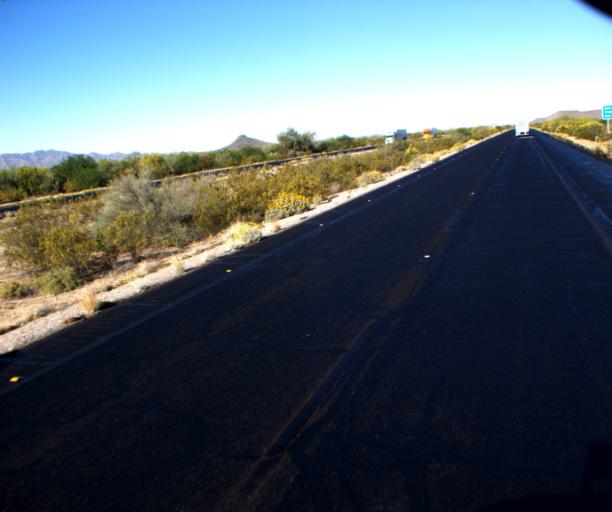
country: US
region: Arizona
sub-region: Pinal County
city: Maricopa
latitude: 32.8435
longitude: -112.2659
